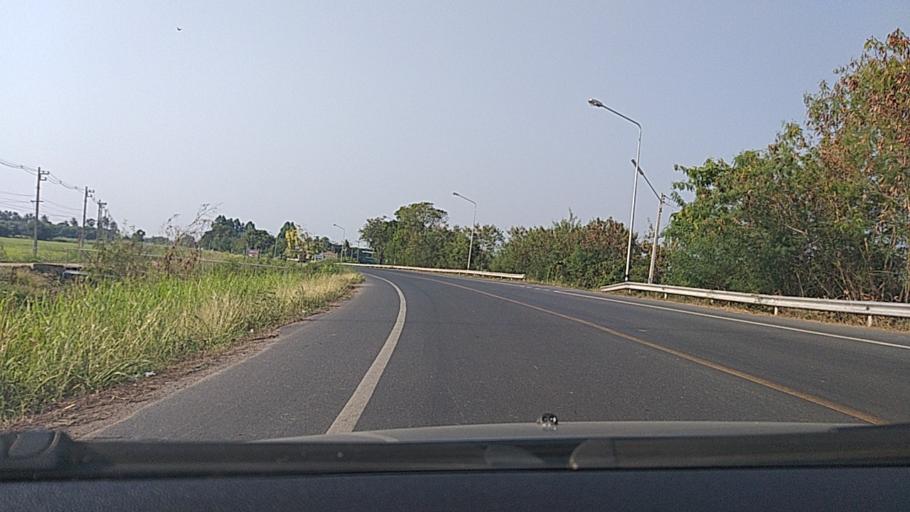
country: TH
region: Sing Buri
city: Phrom Buri
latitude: 14.8132
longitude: 100.4353
